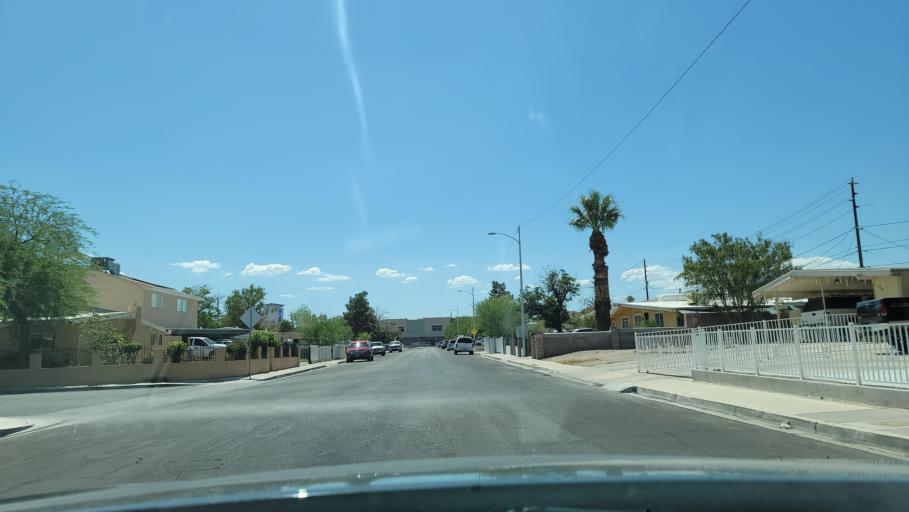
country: US
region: Nevada
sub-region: Clark County
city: Las Vegas
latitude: 36.1771
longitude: -115.1188
